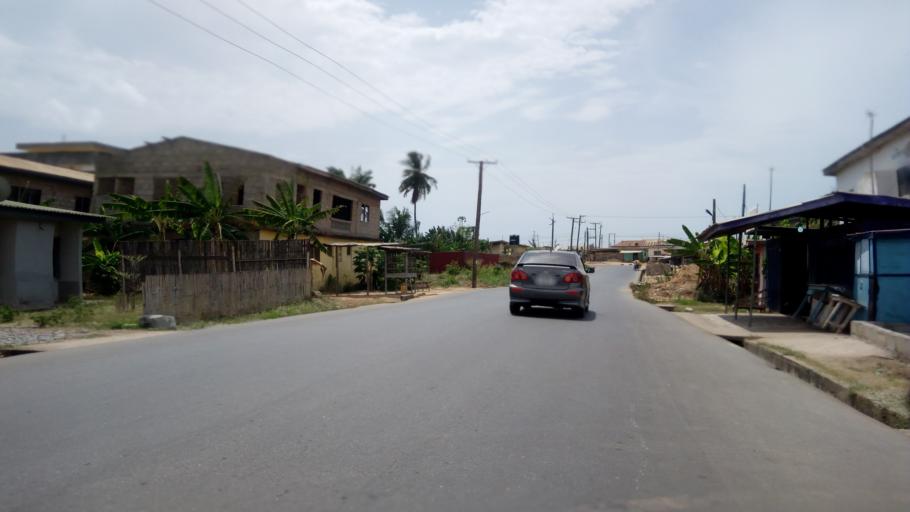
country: GH
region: Central
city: Cape Coast
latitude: 5.1273
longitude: -1.2741
